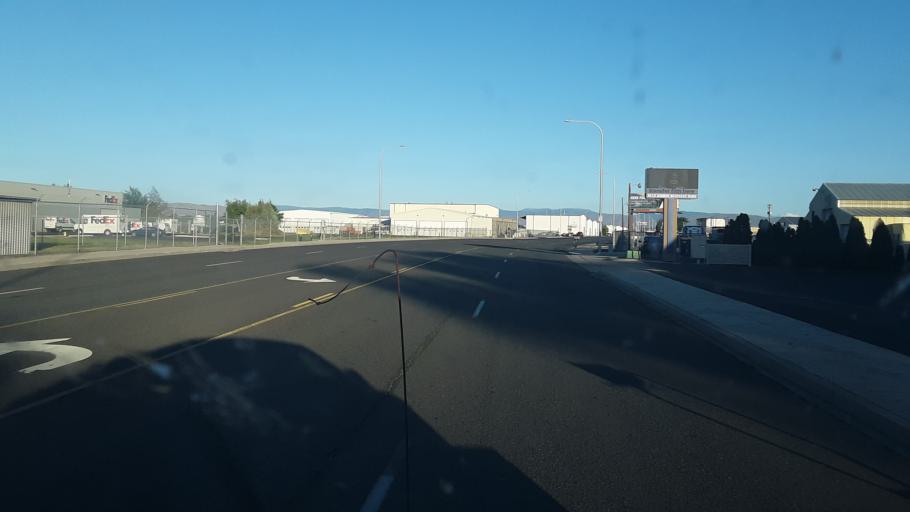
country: US
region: Washington
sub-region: Yakima County
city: Yakima
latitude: 46.5734
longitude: -120.5481
